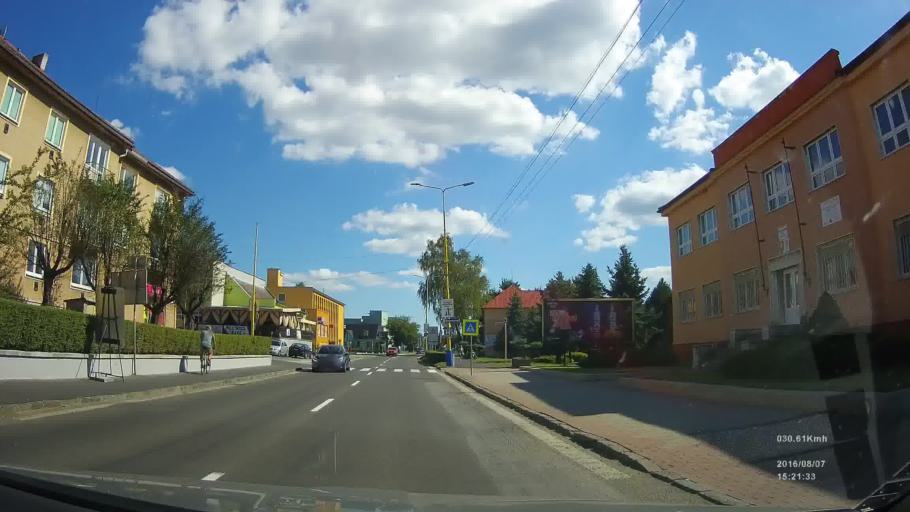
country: SK
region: Presovsky
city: Stropkov
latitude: 49.1994
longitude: 21.6522
